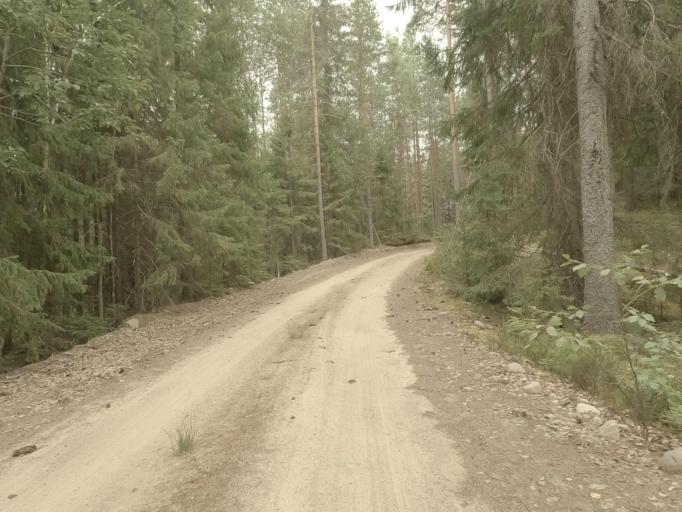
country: RU
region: Leningrad
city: Kamennogorsk
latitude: 61.0405
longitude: 29.1874
